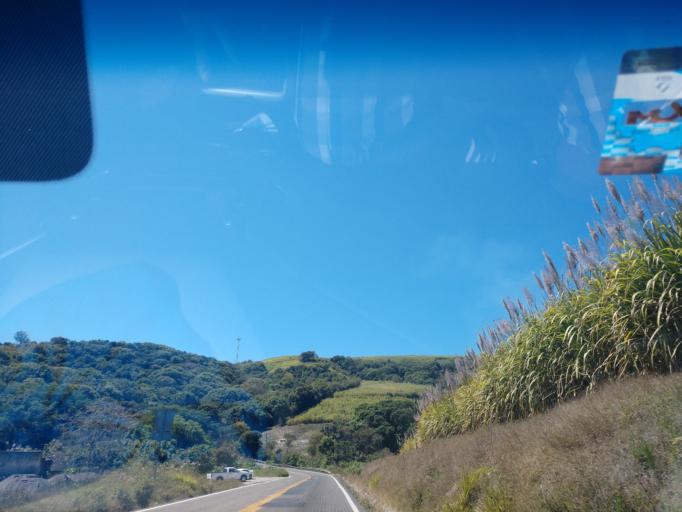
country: MX
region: Nayarit
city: Xalisco
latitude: 21.3641
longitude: -104.9188
